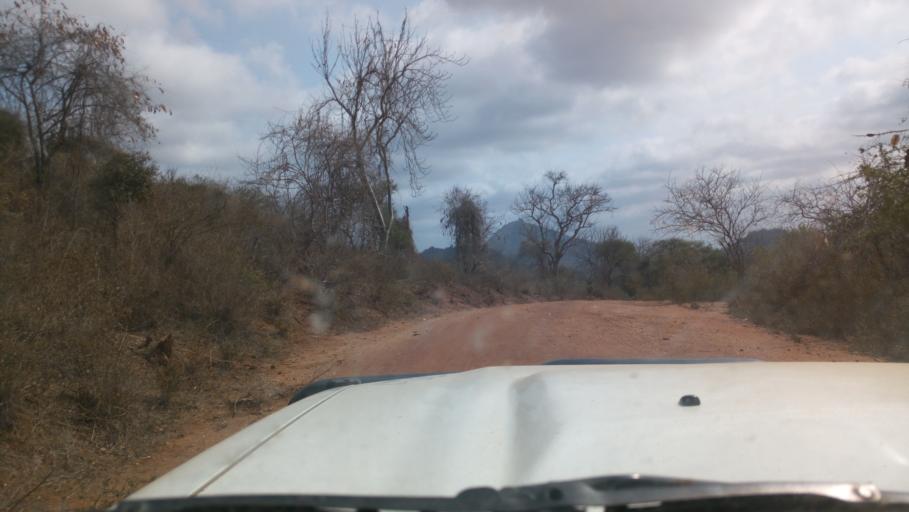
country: KE
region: Kitui
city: Kitui
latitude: -1.8512
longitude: 38.2935
